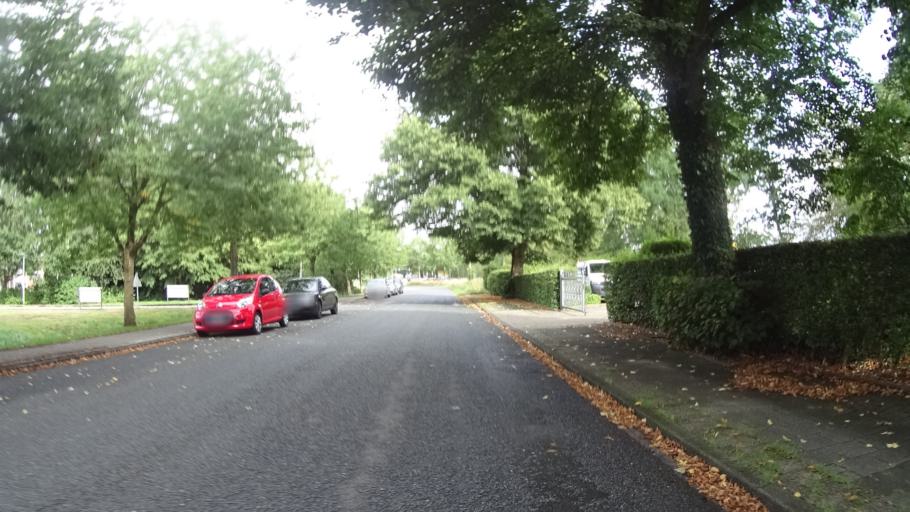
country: DE
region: Lower Saxony
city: Varel
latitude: 53.3996
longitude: 8.1187
